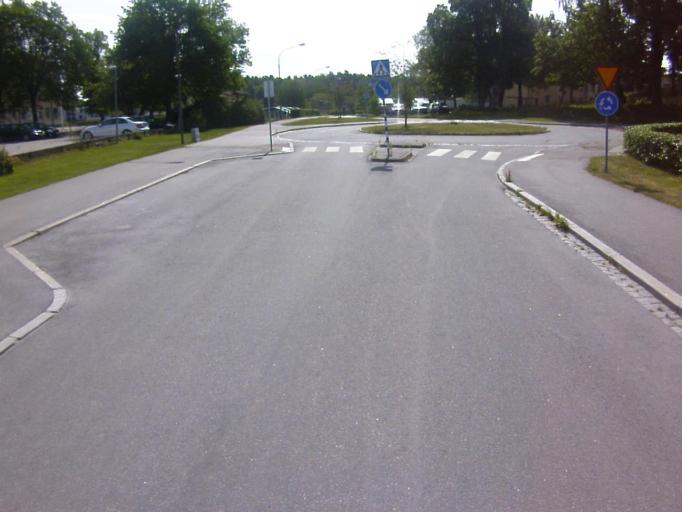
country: SE
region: Soedermanland
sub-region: Eskilstuna Kommun
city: Eskilstuna
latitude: 59.3591
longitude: 16.5259
